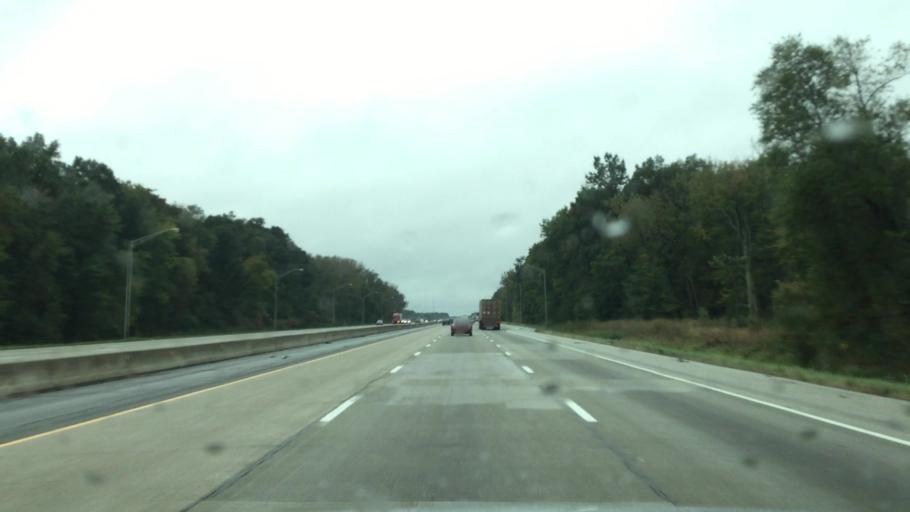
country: US
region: Indiana
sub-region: Porter County
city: Chesterton
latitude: 41.6475
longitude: -86.9862
